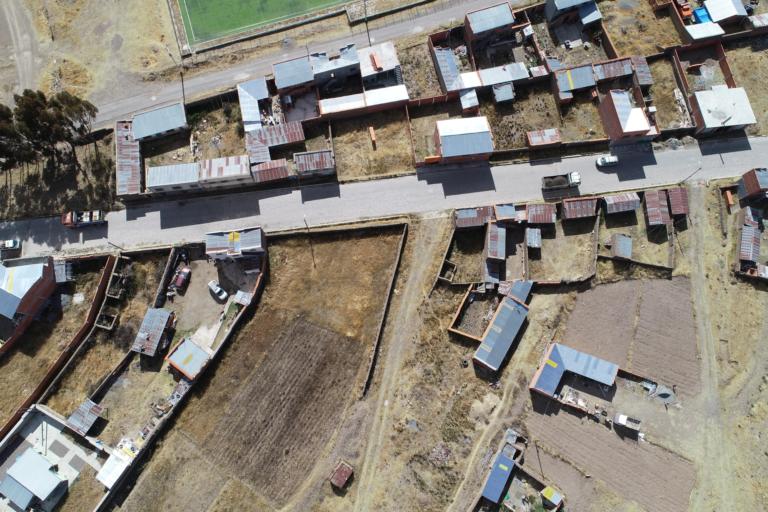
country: BO
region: La Paz
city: Achacachi
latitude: -15.8963
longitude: -68.9088
